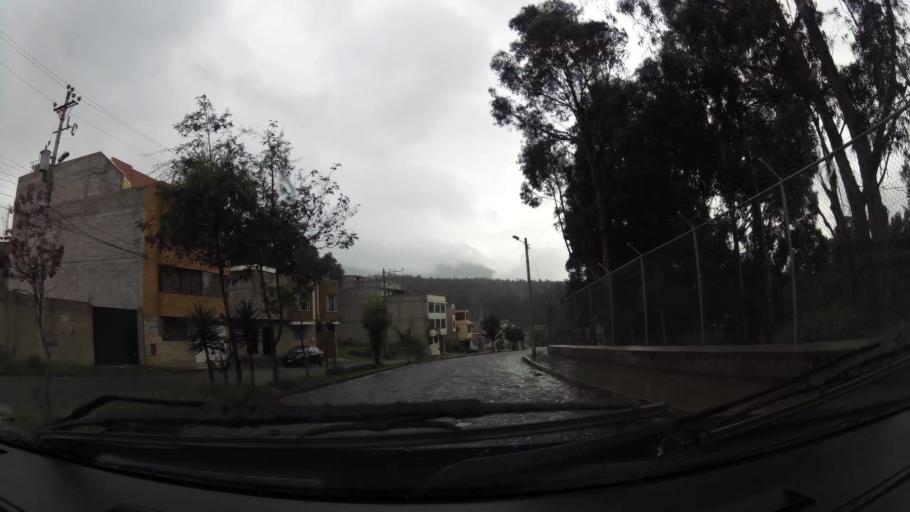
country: EC
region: Pichincha
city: Quito
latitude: -0.0960
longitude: -78.4991
